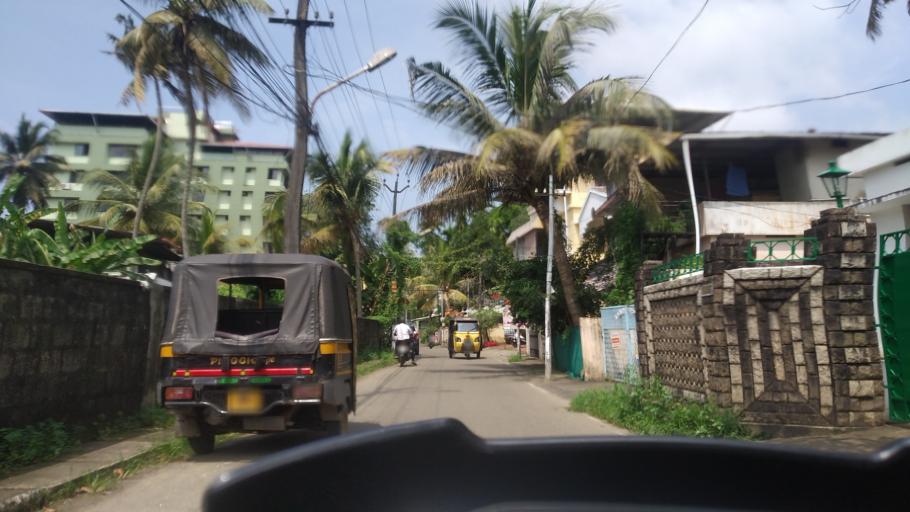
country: IN
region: Kerala
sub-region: Ernakulam
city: Cochin
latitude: 9.9880
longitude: 76.2978
